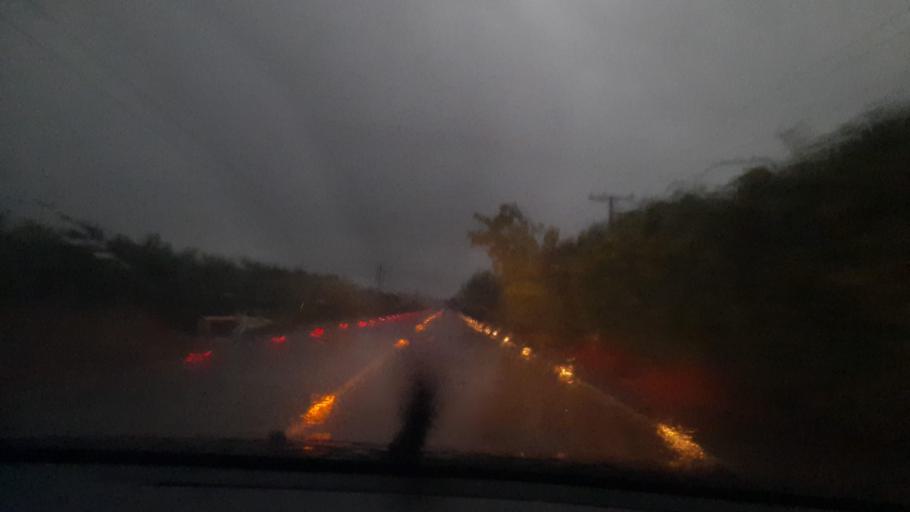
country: HN
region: Cortes
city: Potrerillos
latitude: 15.6406
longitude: -88.4204
